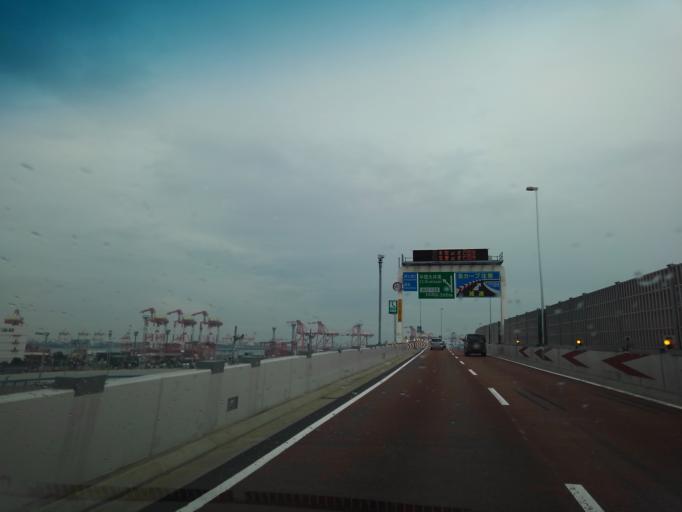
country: JP
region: Kanagawa
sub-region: Kawasaki-shi
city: Kawasaki
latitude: 35.6065
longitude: 139.7537
